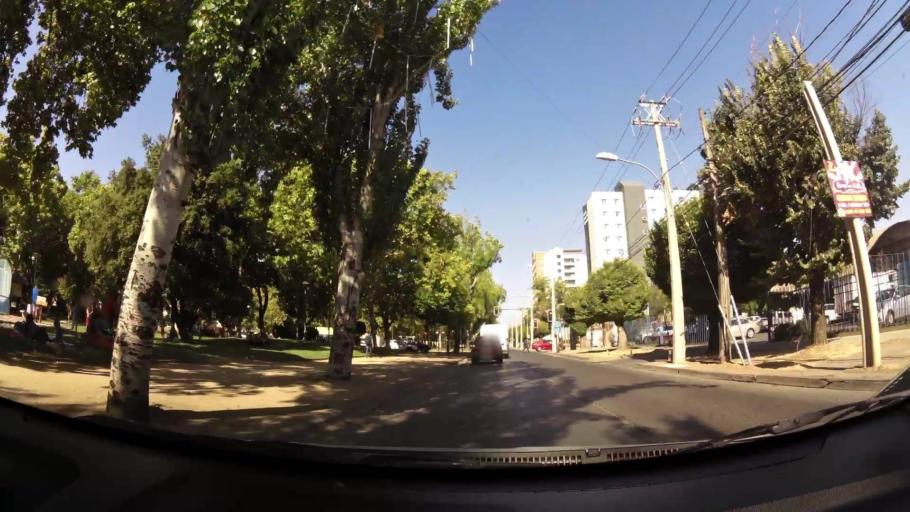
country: CL
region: Maule
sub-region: Provincia de Talca
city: Talca
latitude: -35.4224
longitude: -71.6628
